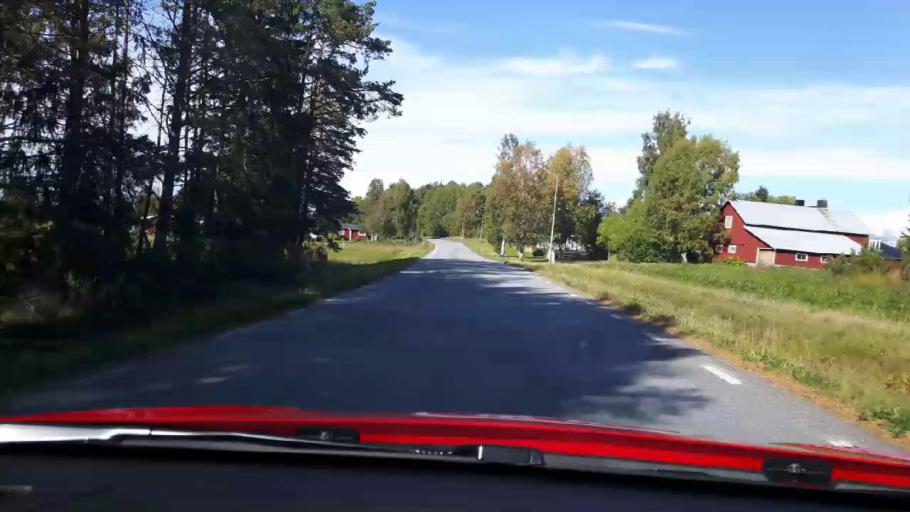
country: SE
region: Jaemtland
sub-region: OEstersunds Kommun
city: Ostersund
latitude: 63.0504
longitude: 14.4516
